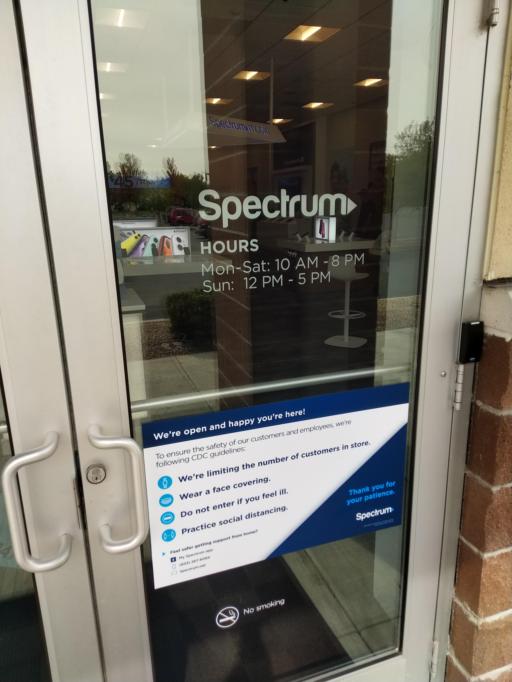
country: US
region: Colorado
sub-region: Mesa County
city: Redlands
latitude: 39.0958
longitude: -108.6044
